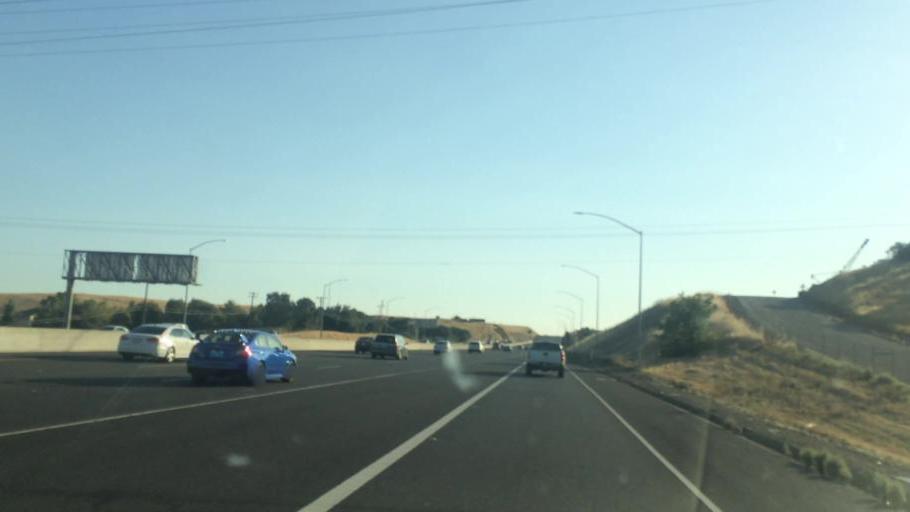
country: US
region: California
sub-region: El Dorado County
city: El Dorado Hills
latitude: 38.6513
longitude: -121.0759
